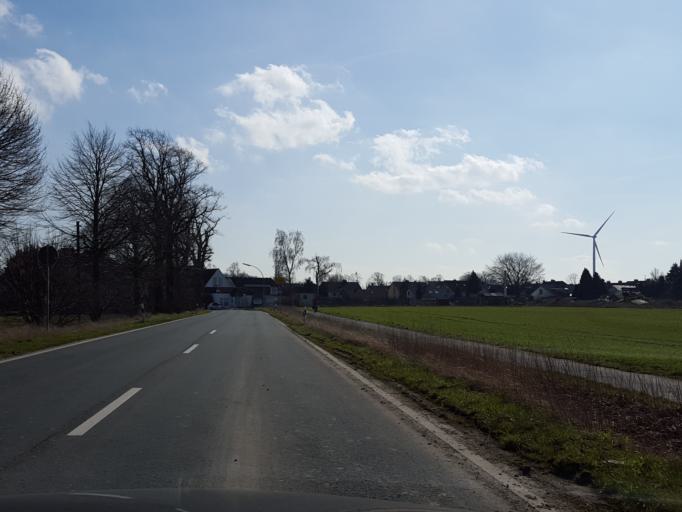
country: DE
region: North Rhine-Westphalia
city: Oer-Erkenschwick
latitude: 51.6334
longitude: 7.2886
